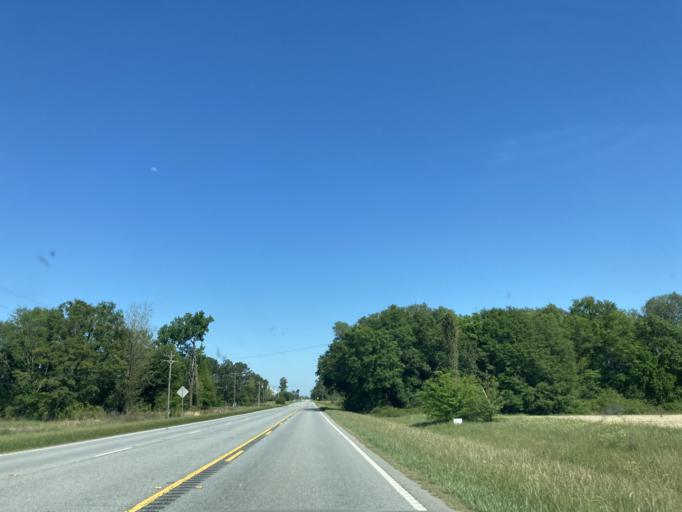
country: US
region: Georgia
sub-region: Miller County
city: Colquitt
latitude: 31.1856
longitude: -84.6112
